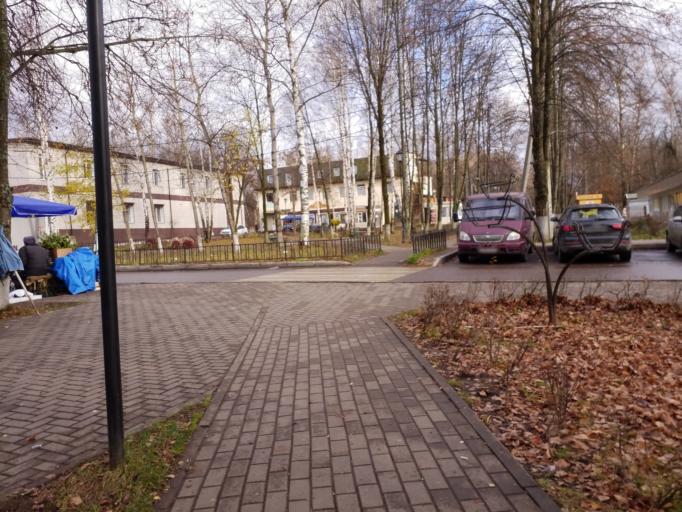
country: RU
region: Moskovskaya
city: Ashukino
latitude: 56.1617
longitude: 37.9452
